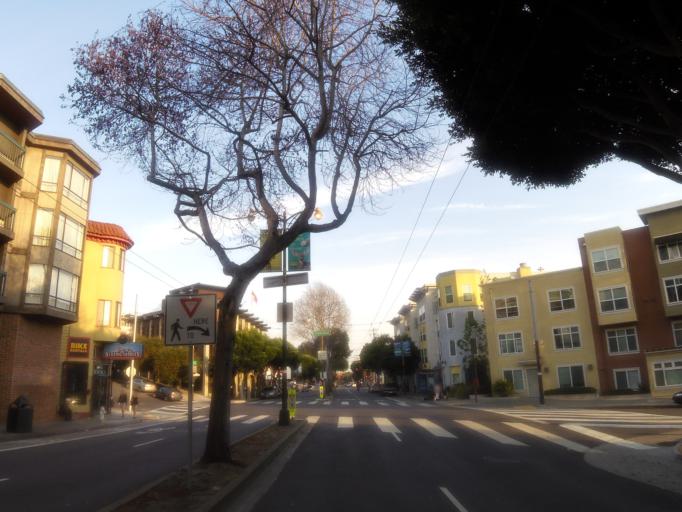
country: US
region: California
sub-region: San Francisco County
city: San Francisco
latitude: 37.8042
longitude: -122.4157
